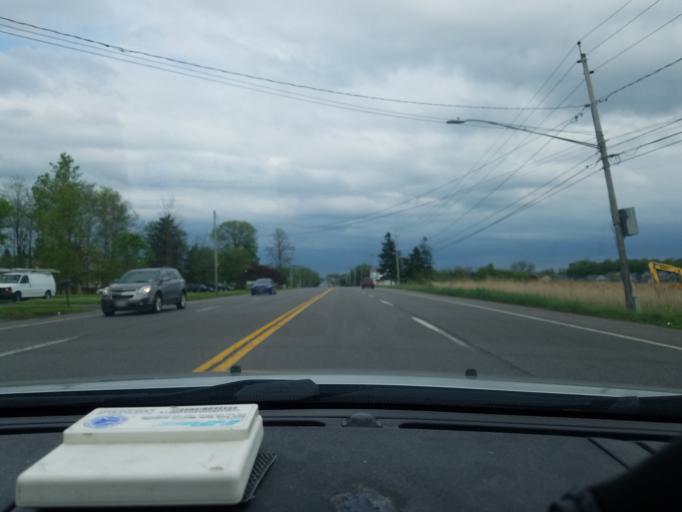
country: US
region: New York
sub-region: Onondaga County
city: Galeville
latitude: 43.1212
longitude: -76.1729
